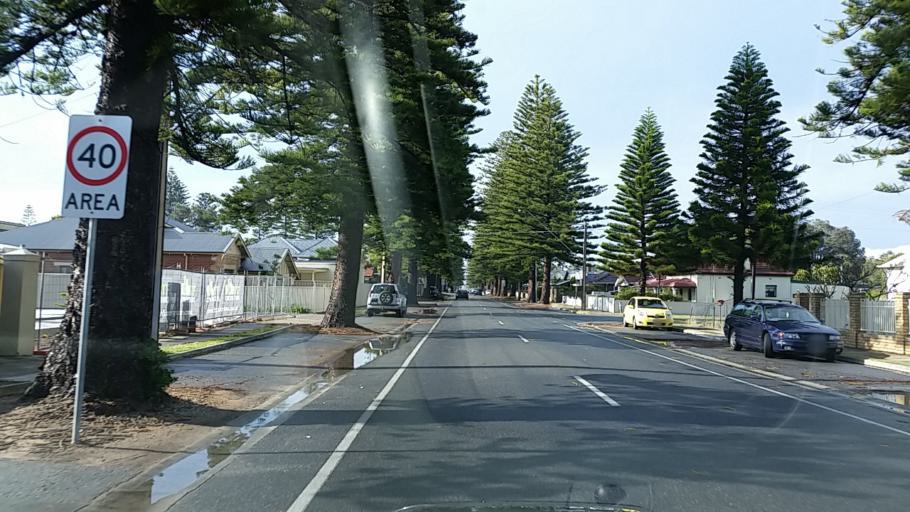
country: AU
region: South Australia
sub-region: Charles Sturt
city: Henley Beach
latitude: -34.9212
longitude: 138.4973
